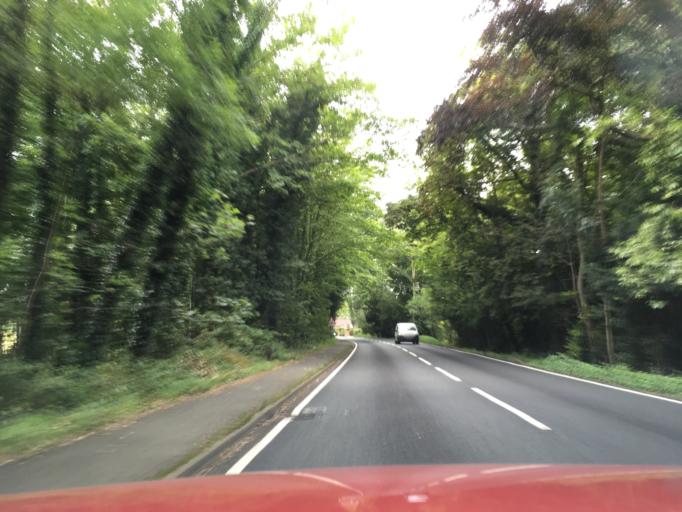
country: GB
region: England
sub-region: Kent
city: Cranbrook
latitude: 51.1086
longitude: 0.5504
